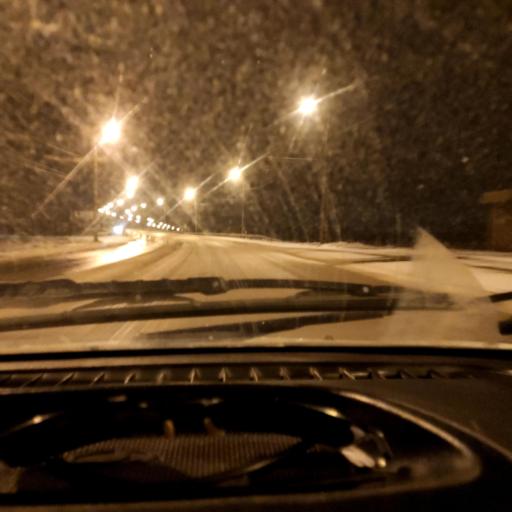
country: RU
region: Samara
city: Zhigulevsk
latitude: 53.5132
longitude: 49.5301
